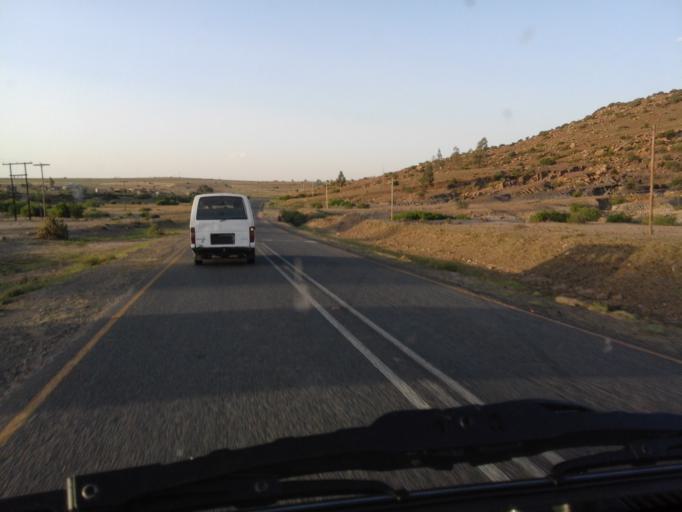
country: LS
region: Mafeteng
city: Mafeteng
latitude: -29.8722
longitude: 27.2380
